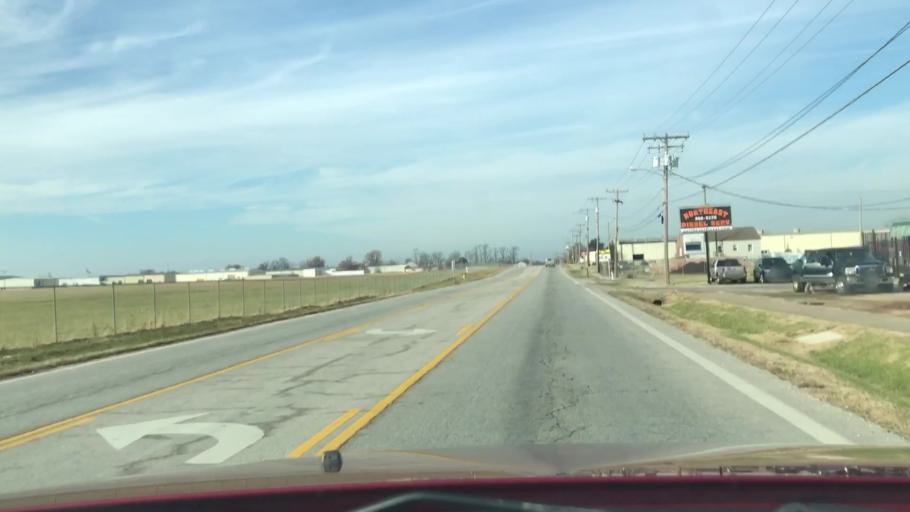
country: US
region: Missouri
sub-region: Greene County
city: Springfield
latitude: 37.2253
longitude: -93.2518
